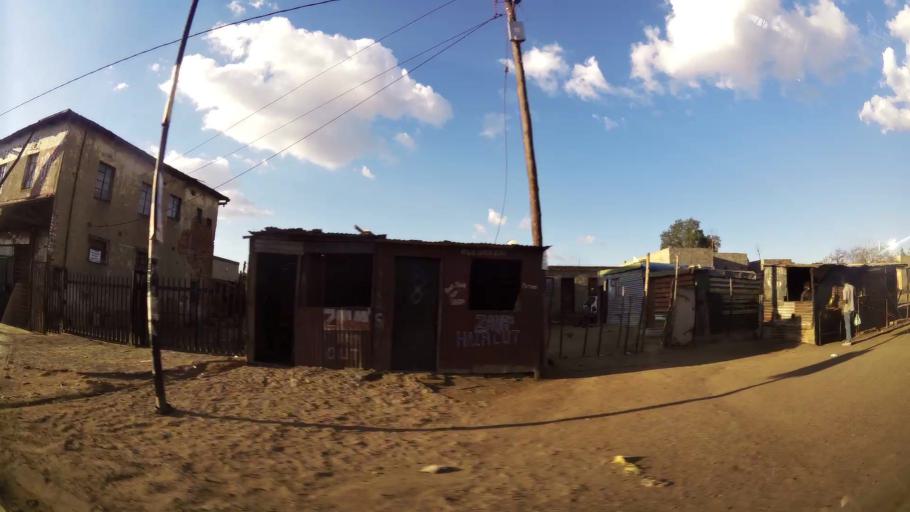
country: ZA
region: Mpumalanga
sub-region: Nkangala District Municipality
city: Witbank
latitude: -25.8743
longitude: 29.1973
